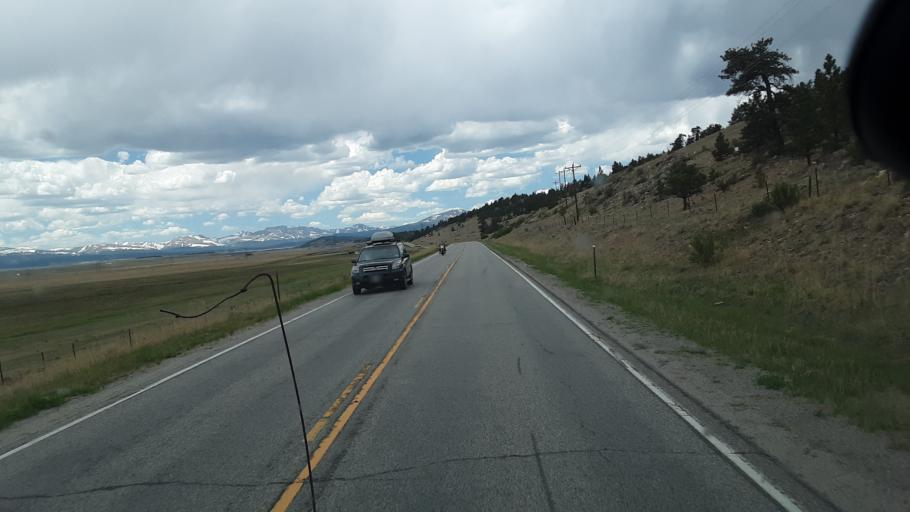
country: US
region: Colorado
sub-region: Park County
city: Fairplay
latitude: 39.0664
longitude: -105.8565
